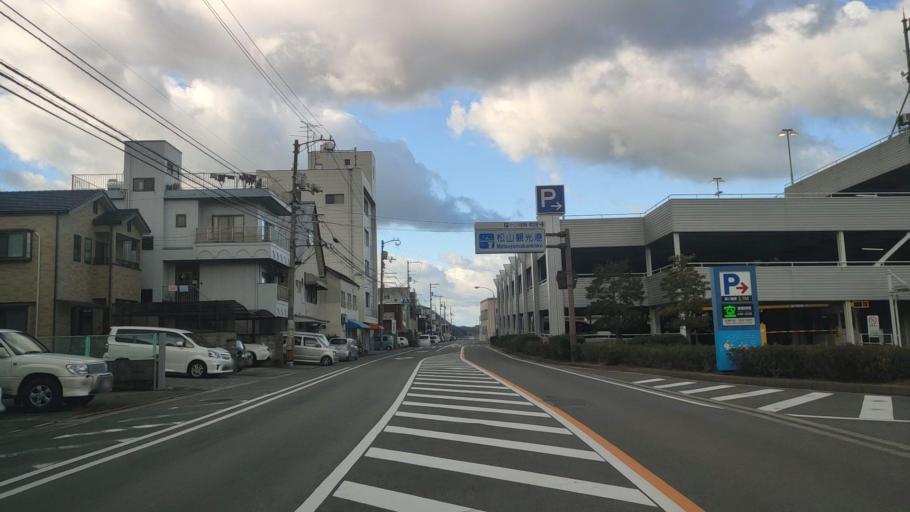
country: JP
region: Ehime
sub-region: Shikoku-chuo Shi
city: Matsuyama
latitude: 33.8881
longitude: 132.7039
